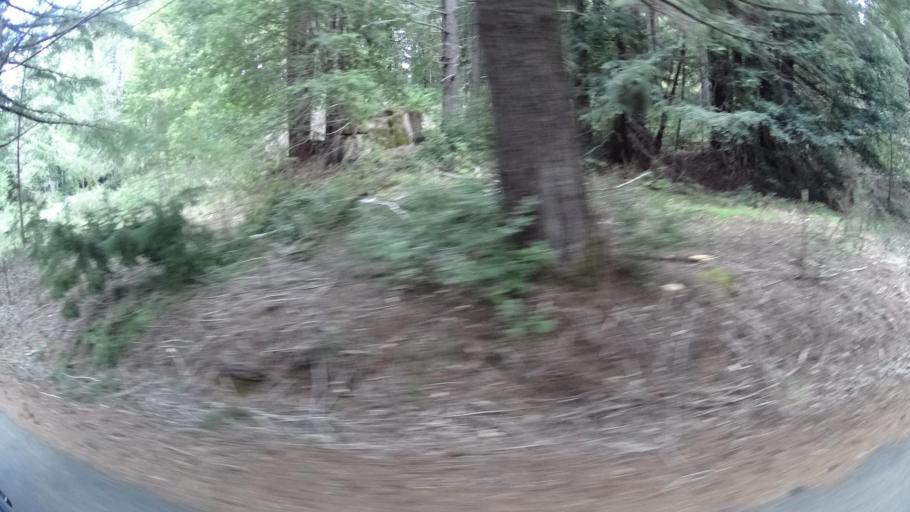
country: US
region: California
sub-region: Humboldt County
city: Redway
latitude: 40.0315
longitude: -123.9517
